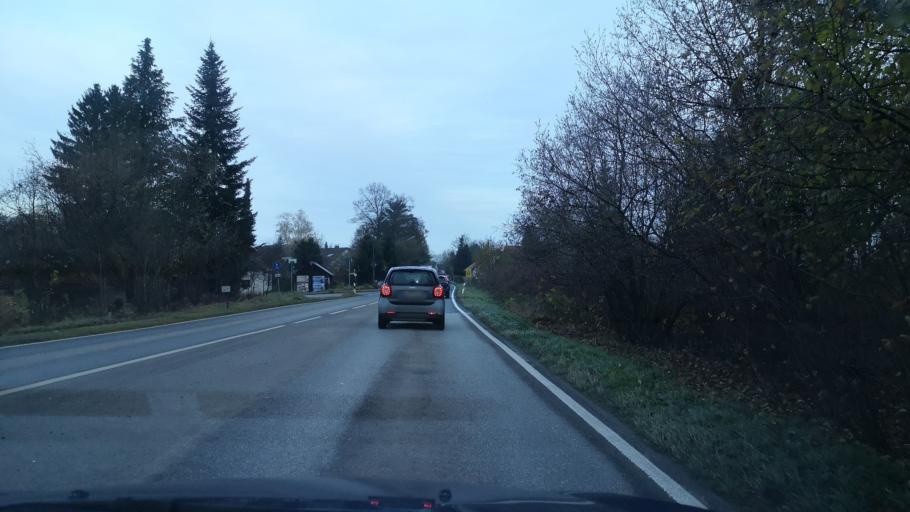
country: DE
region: Bavaria
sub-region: Upper Bavaria
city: Forstinning
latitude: 48.1562
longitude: 11.9035
